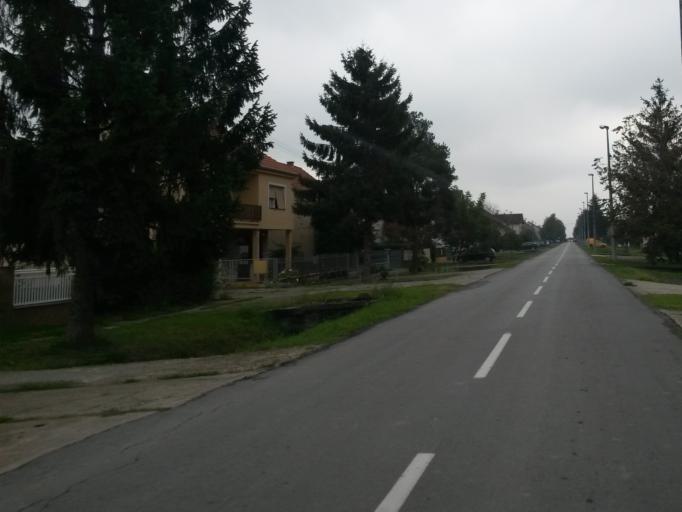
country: HR
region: Osjecko-Baranjska
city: Brijest
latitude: 45.5223
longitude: 18.6277
